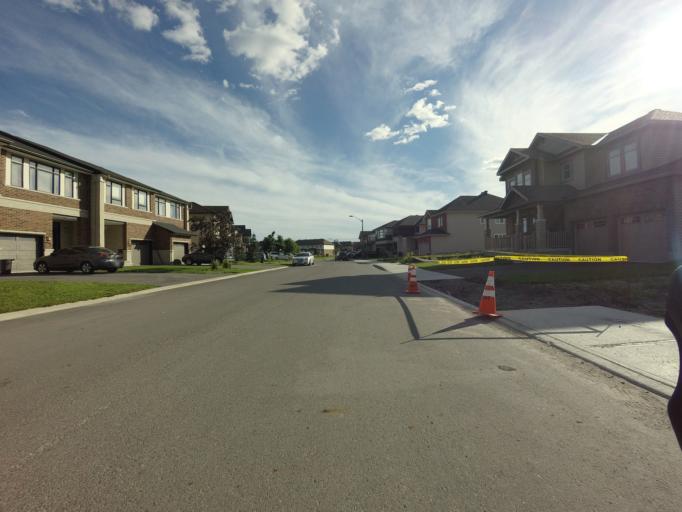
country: CA
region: Ontario
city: Ottawa
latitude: 45.2872
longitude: -75.6670
